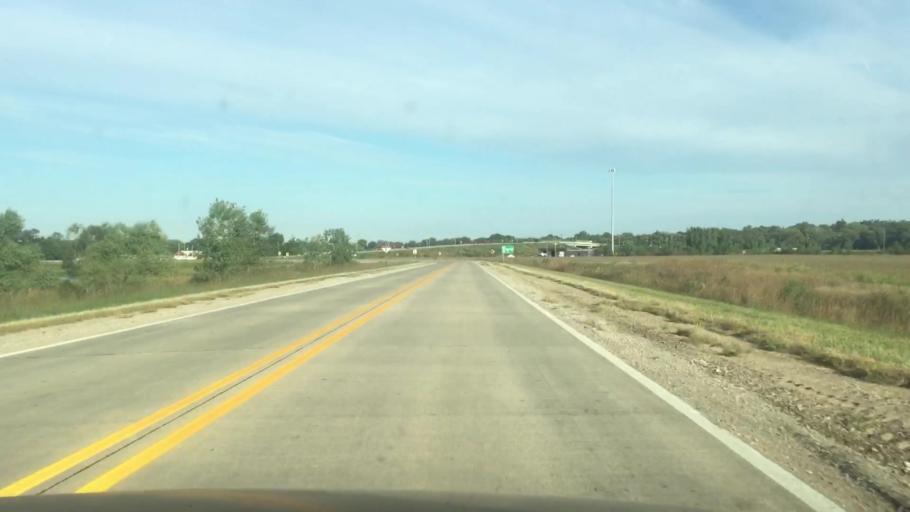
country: US
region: Nebraska
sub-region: Jefferson County
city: Fairbury
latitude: 40.1272
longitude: -97.1652
